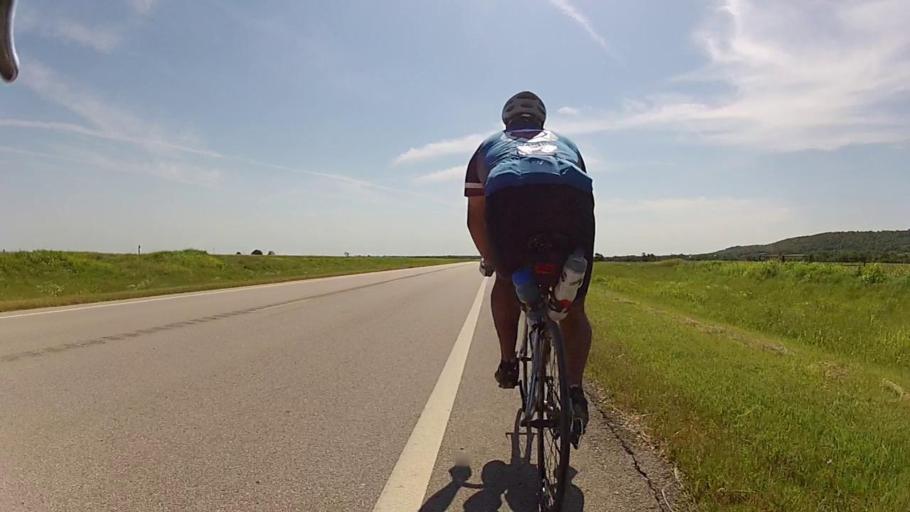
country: US
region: Kansas
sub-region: Chautauqua County
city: Sedan
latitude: 37.1067
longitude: -96.5483
